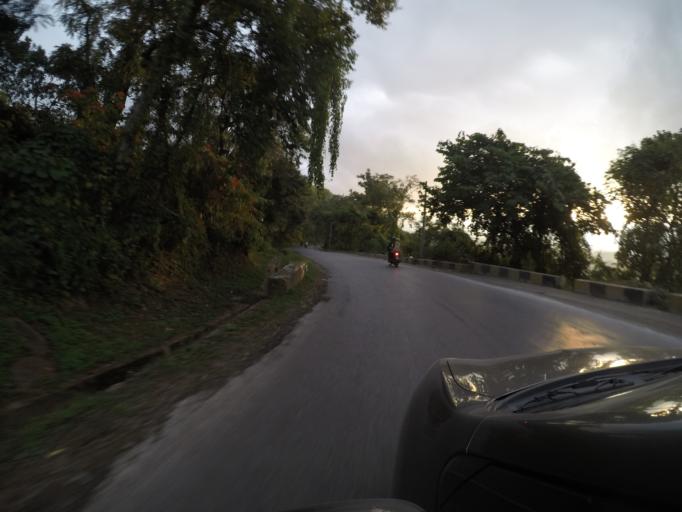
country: MM
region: Shan
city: Taunggyi
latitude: 20.7976
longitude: 97.0194
